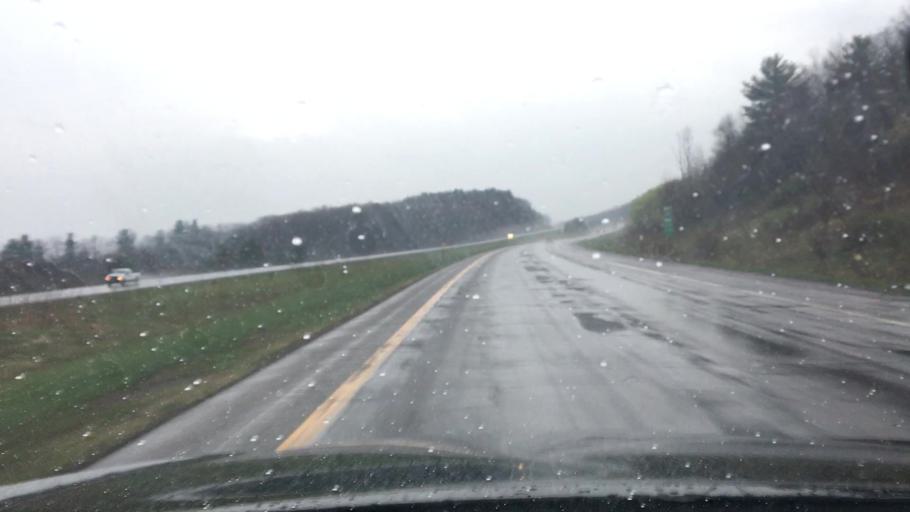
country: US
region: New York
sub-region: Chautauqua County
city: Lakewood
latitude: 42.1300
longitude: -79.3233
